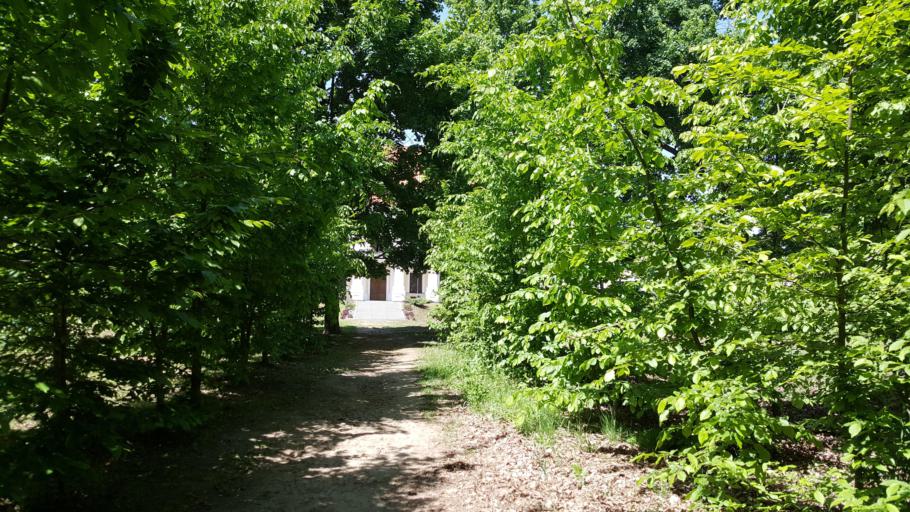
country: BY
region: Brest
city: Brest
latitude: 52.1550
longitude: 23.6382
